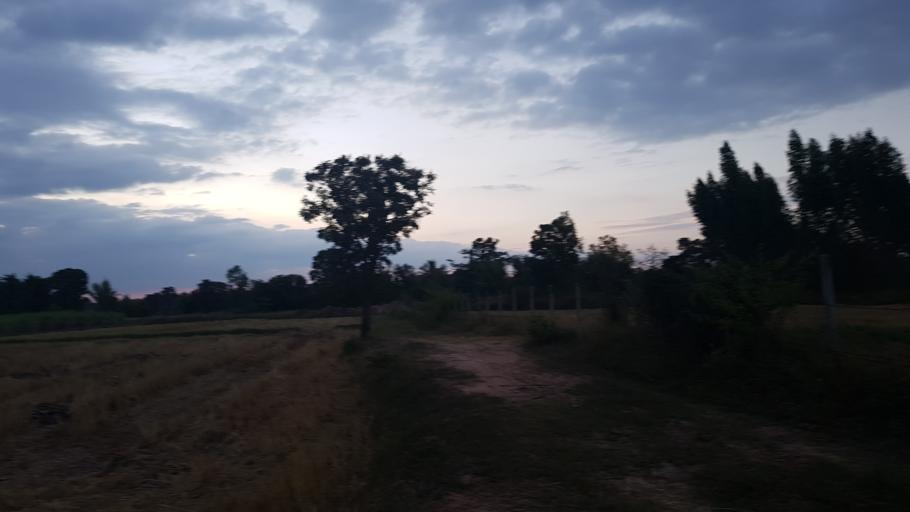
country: TH
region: Nakhon Ratchasima
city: Bua Lai
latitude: 15.6550
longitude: 102.5358
